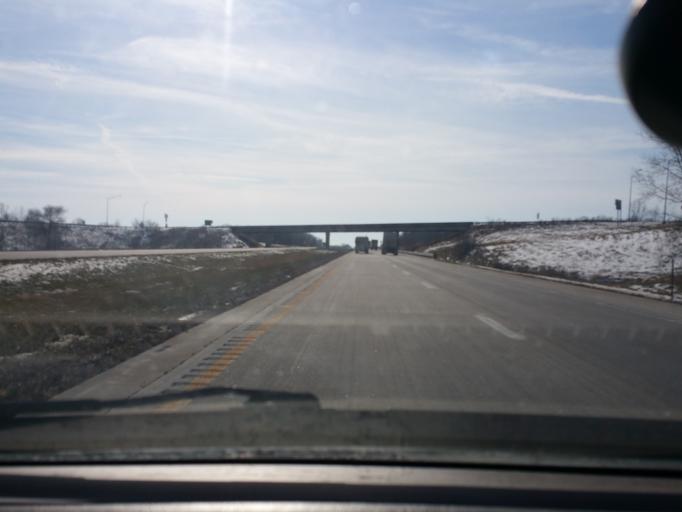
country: US
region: Missouri
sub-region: Clinton County
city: Cameron
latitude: 39.6698
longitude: -94.2352
